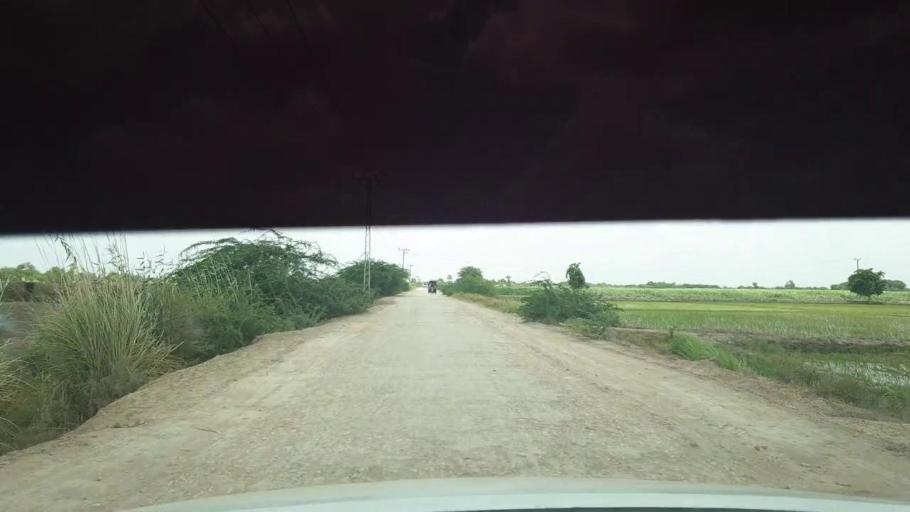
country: PK
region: Sindh
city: Kadhan
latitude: 24.4651
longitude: 69.0001
